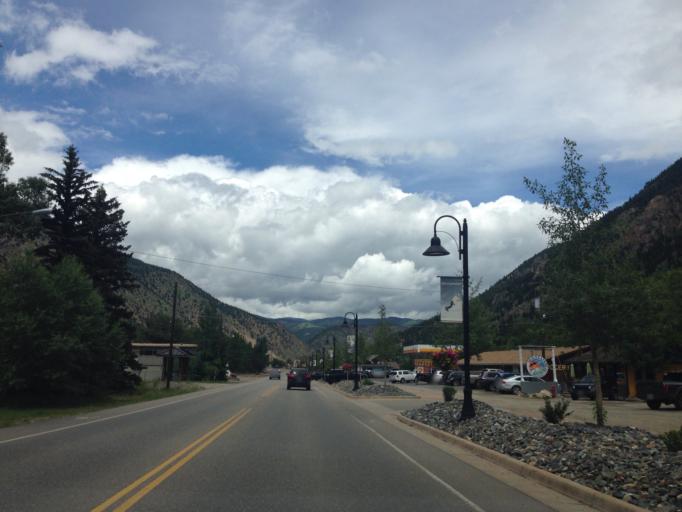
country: US
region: Colorado
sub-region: Clear Creek County
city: Georgetown
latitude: 39.7117
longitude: -105.6961
